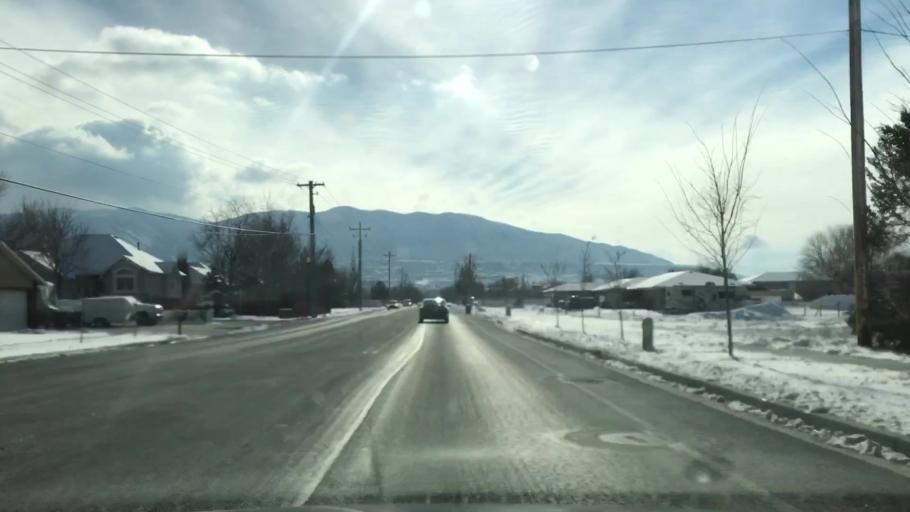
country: US
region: Utah
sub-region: Salt Lake County
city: Draper
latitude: 40.5178
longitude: -111.8818
